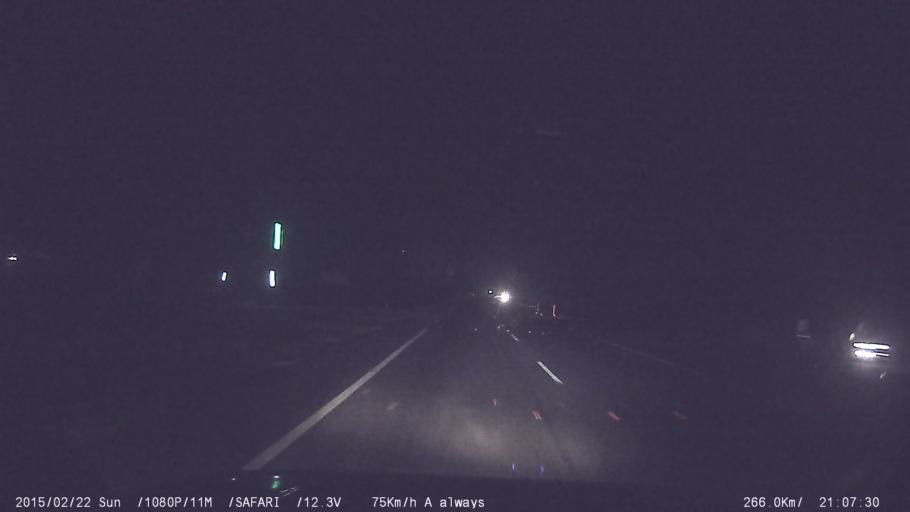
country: IN
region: Tamil Nadu
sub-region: Karur
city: Pallappatti
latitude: 10.7229
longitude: 77.9280
